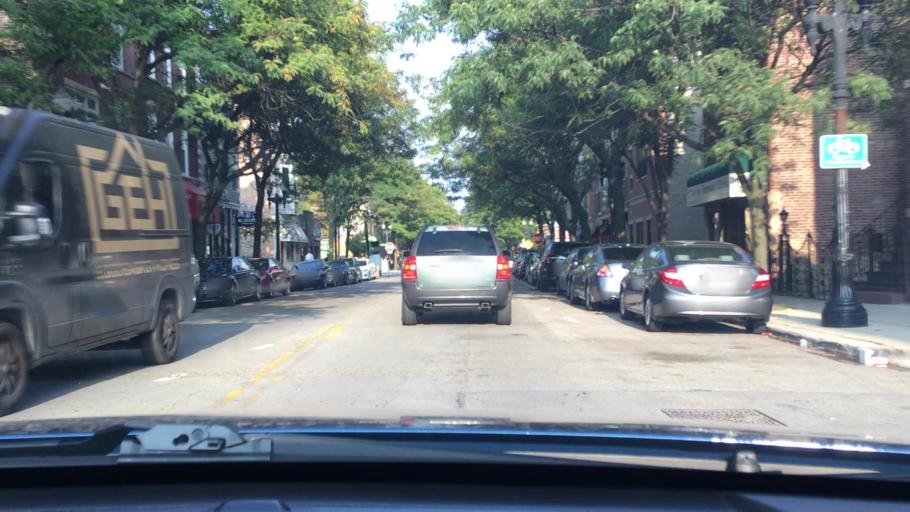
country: US
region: Illinois
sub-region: Cook County
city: Chicago
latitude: 41.8694
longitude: -87.6563
